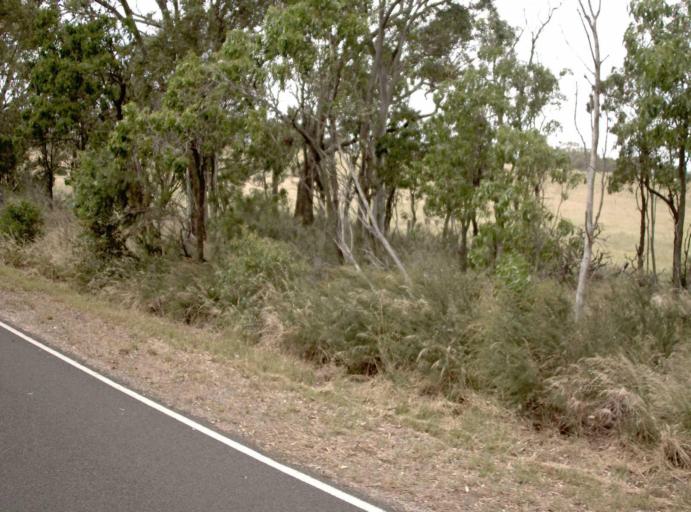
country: AU
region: Victoria
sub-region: Wellington
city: Sale
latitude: -37.9806
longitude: 147.1714
